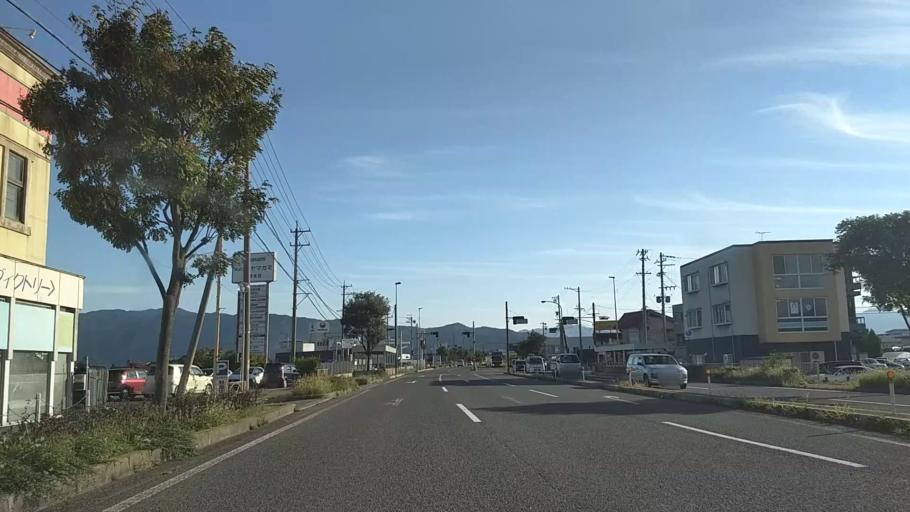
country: JP
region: Nagano
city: Nagano-shi
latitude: 36.6026
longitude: 138.1944
